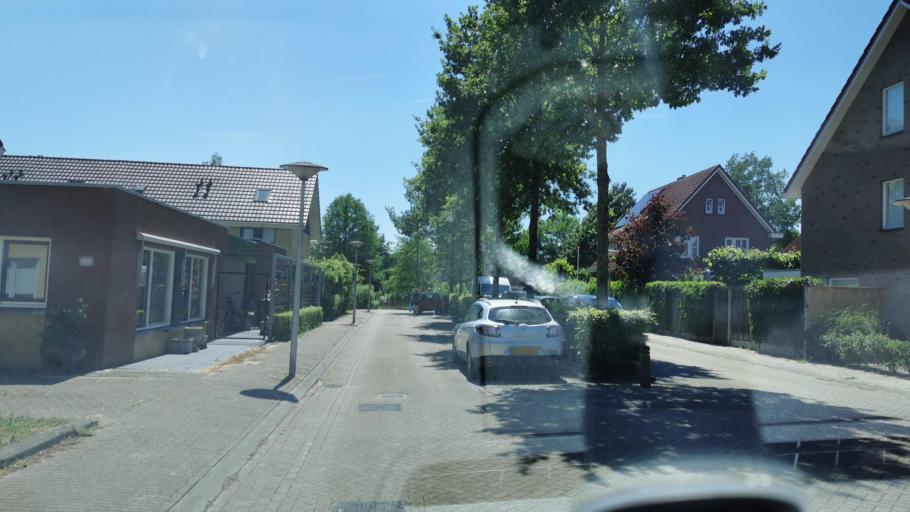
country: NL
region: Overijssel
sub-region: Gemeente Enschede
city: Enschede
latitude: 52.2121
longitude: 6.9588
